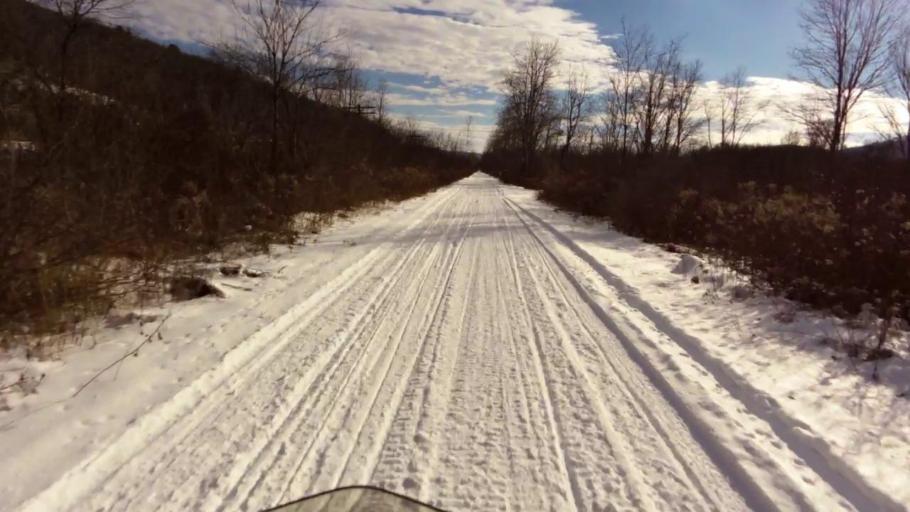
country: US
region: Pennsylvania
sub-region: McKean County
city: Foster Brook
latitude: 42.0184
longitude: -78.6284
